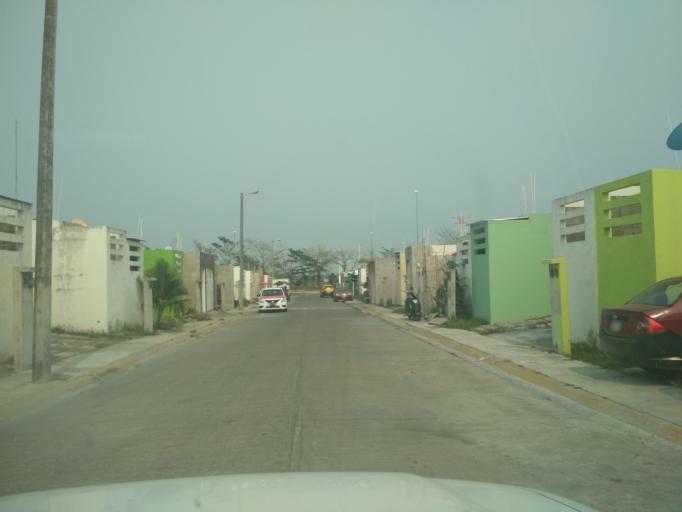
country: MX
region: Veracruz
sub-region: Veracruz
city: Las Amapolas
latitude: 19.1393
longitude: -96.2204
